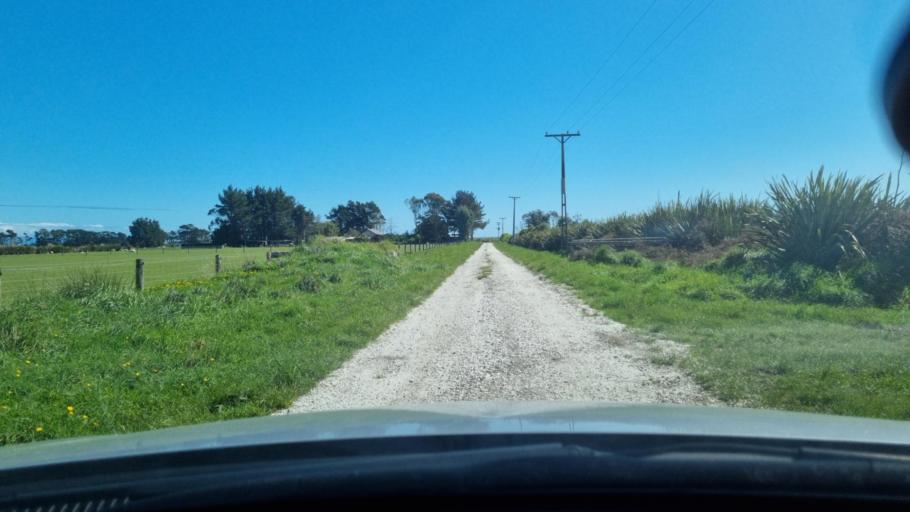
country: NZ
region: Southland
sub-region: Invercargill City
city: Invercargill
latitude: -46.3915
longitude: 168.2950
